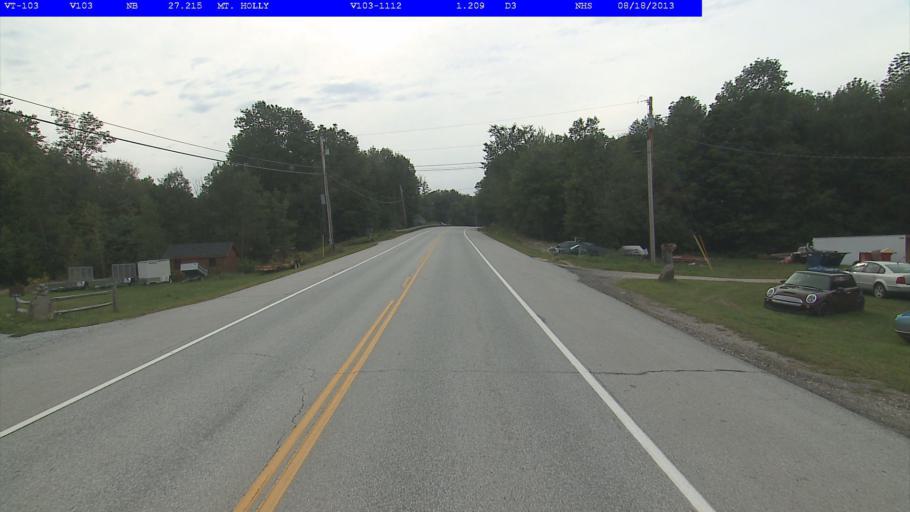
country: US
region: Vermont
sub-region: Windsor County
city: Chester
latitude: 43.4378
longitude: -72.7564
